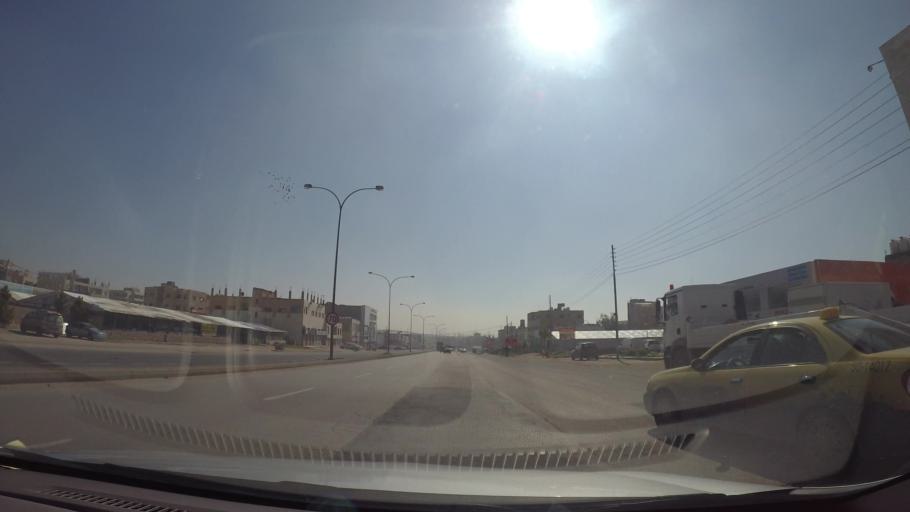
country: JO
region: Amman
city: Al Bunayyat ash Shamaliyah
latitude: 31.8995
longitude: 35.8960
